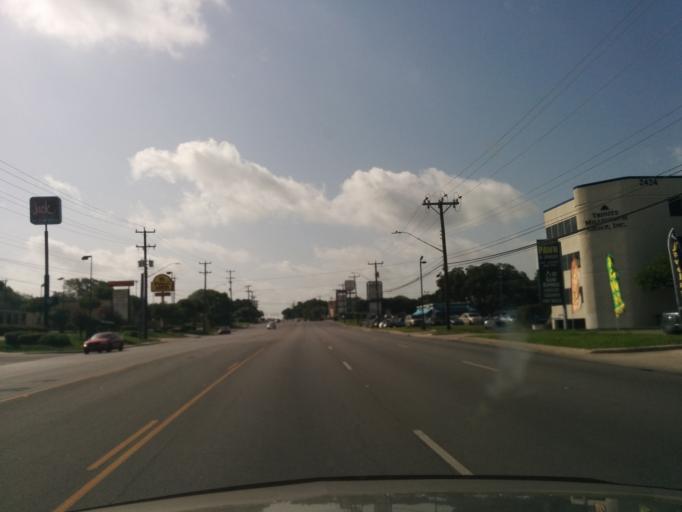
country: US
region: Texas
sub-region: Bexar County
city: Leon Valley
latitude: 29.5064
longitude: -98.5866
